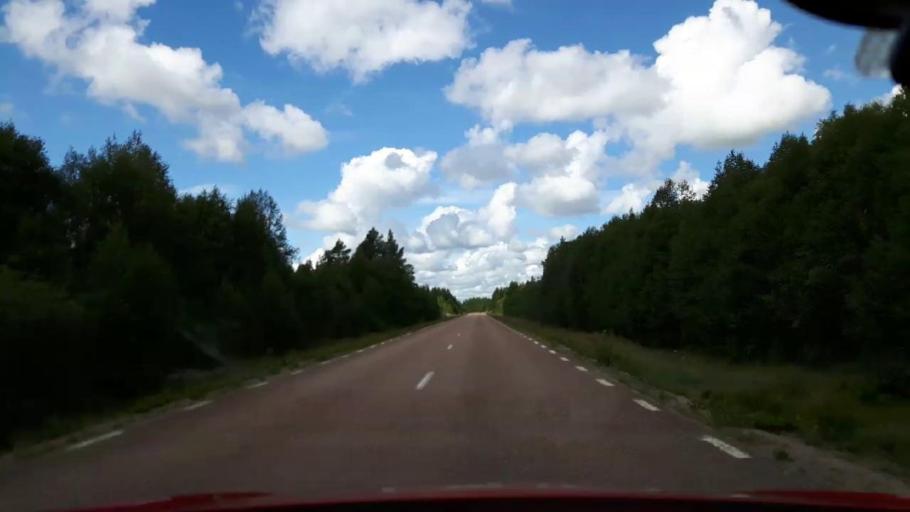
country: SE
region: Dalarna
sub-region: Alvdalens Kommun
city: AElvdalen
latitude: 61.8018
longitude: 13.6636
